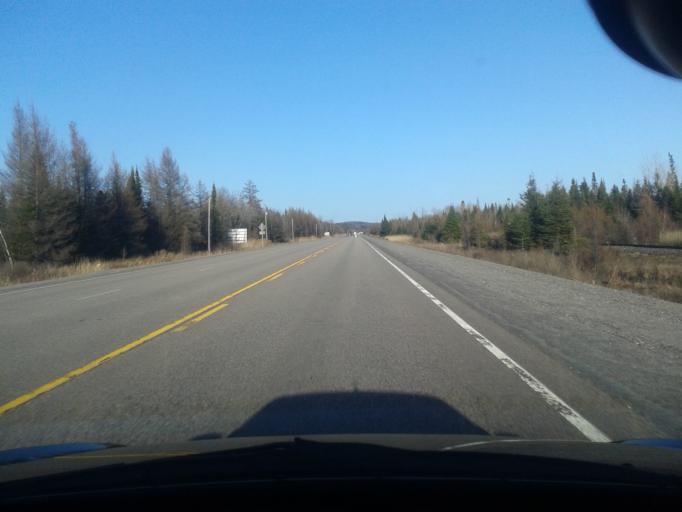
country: CA
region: Ontario
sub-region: Nipissing District
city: North Bay
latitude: 46.3696
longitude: -79.7334
